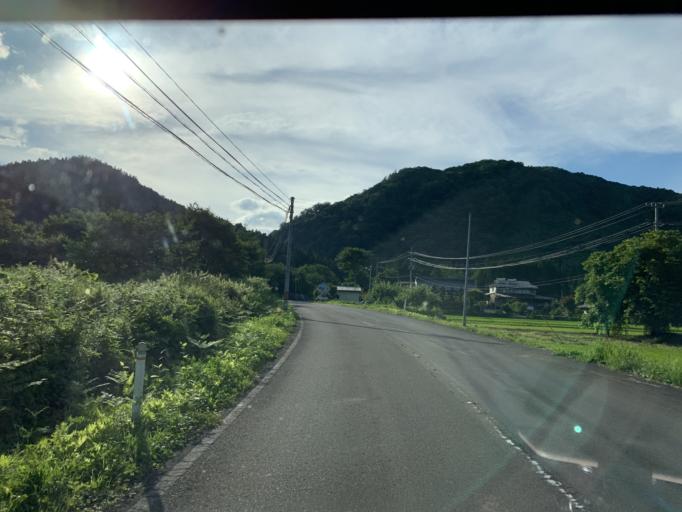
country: JP
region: Iwate
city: Ichinoseki
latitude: 38.9015
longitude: 140.9316
